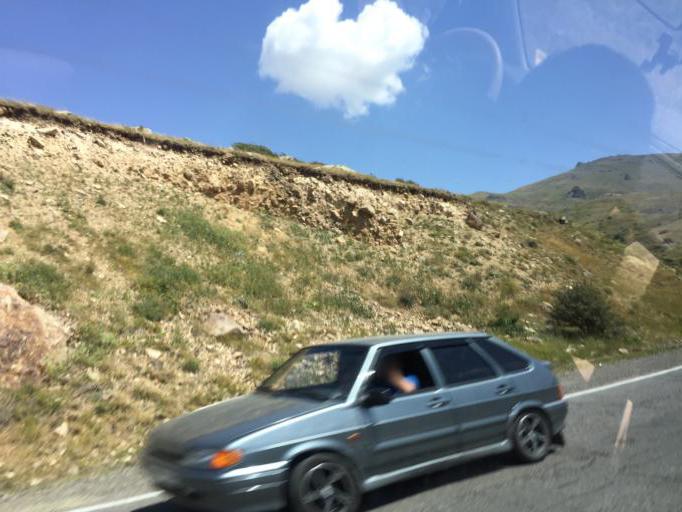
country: AM
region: Vayots' Dzori Marz
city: Jermuk
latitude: 39.7044
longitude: 45.6810
